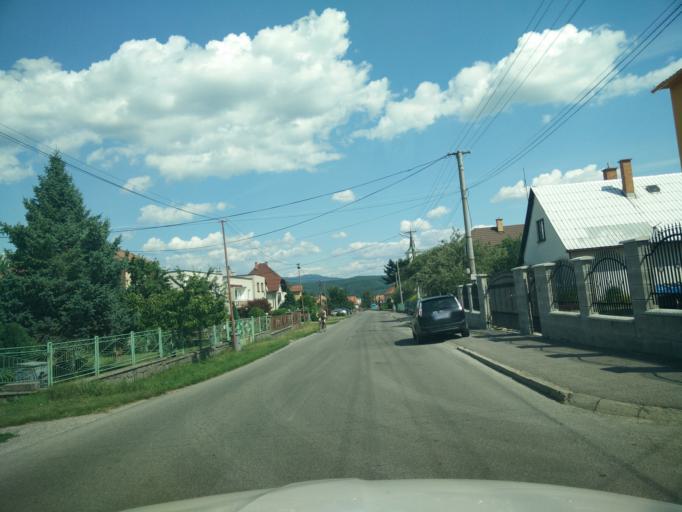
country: SK
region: Nitriansky
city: Prievidza
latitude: 48.8195
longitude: 18.6182
